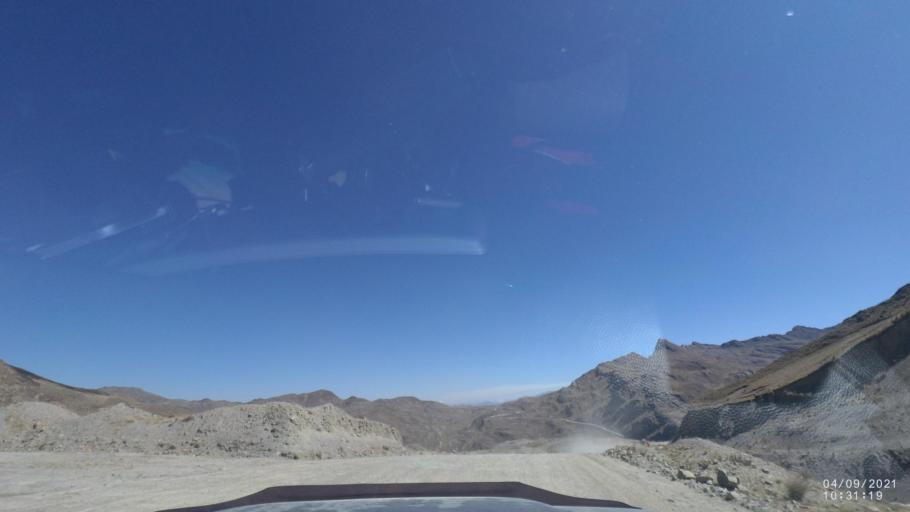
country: BO
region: Cochabamba
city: Sipe Sipe
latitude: -17.3022
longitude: -66.4460
